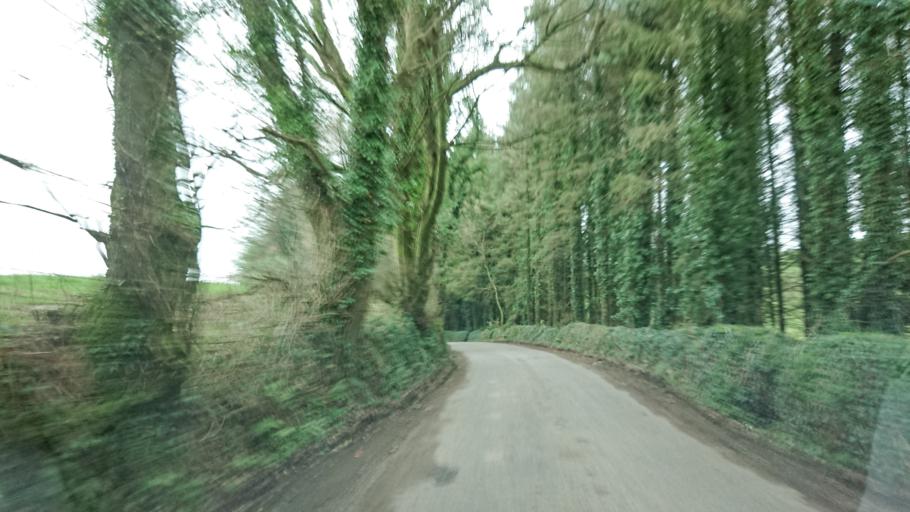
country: IE
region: Munster
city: Carrick-on-Suir
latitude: 52.2714
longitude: -7.4075
